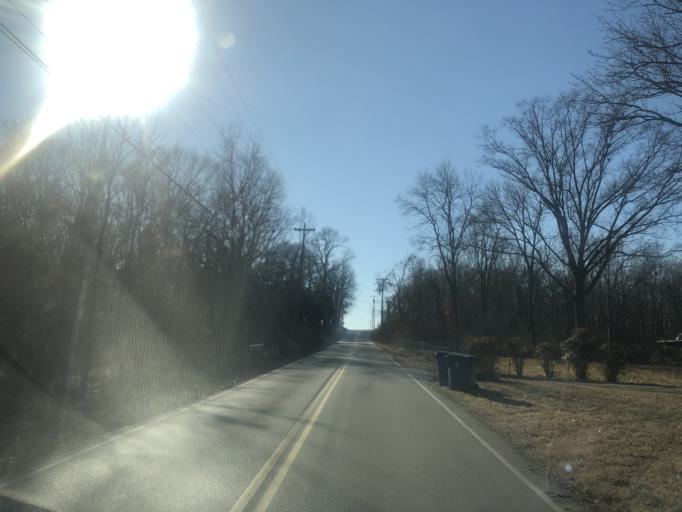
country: US
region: Tennessee
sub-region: Rutherford County
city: La Vergne
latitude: 36.0088
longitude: -86.5830
